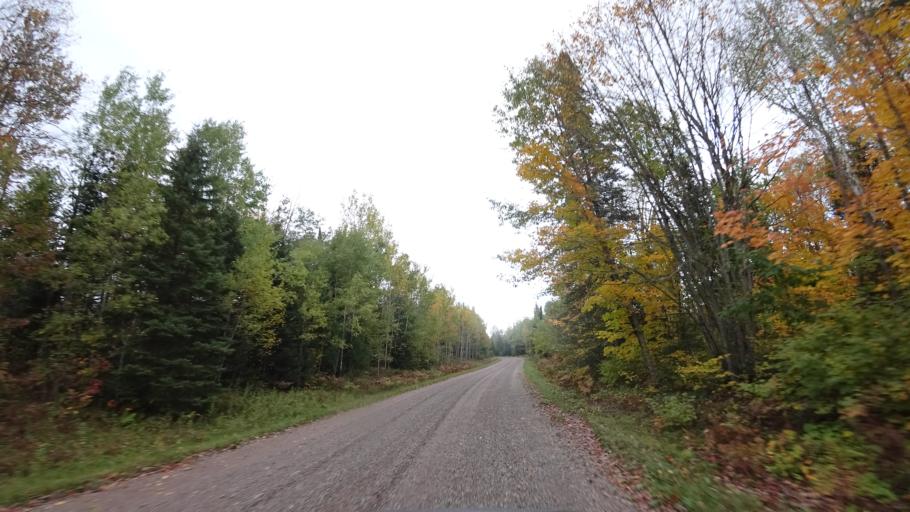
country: US
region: Wisconsin
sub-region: Sawyer County
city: Little Round Lake
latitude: 45.9672
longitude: -90.9816
